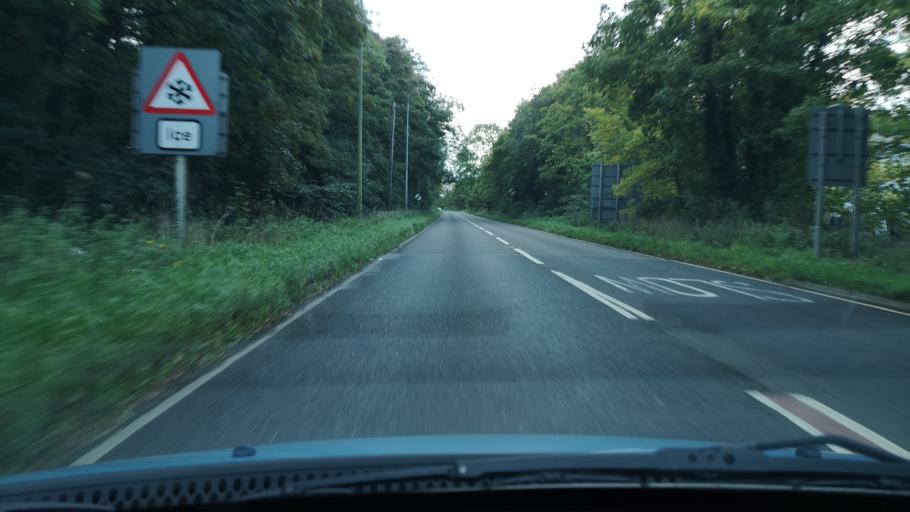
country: GB
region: England
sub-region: North Lincolnshire
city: Crowle
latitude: 53.5865
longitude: -0.8217
